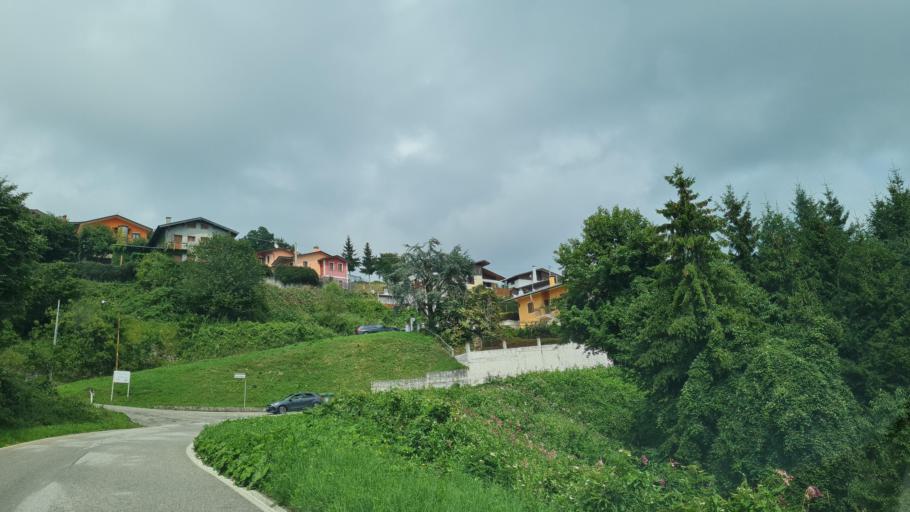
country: IT
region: Veneto
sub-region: Provincia di Vicenza
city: Conco
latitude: 45.8023
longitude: 11.6571
